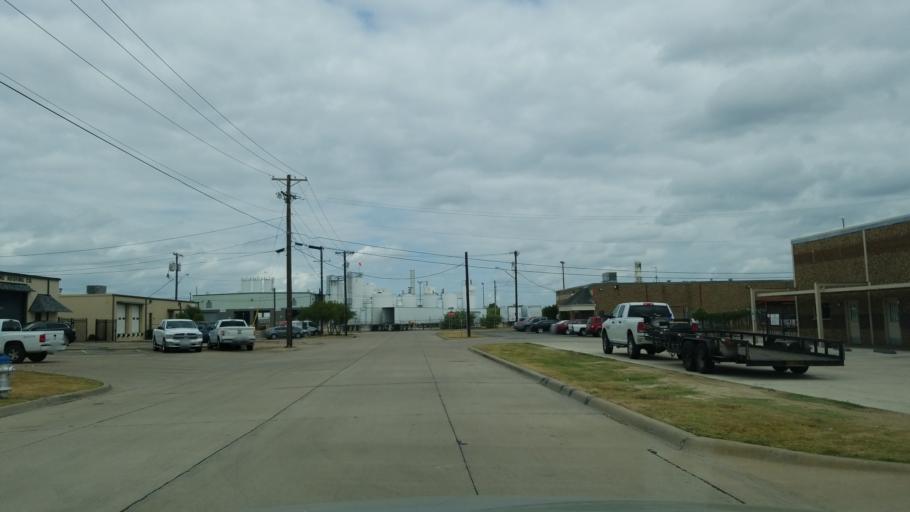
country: US
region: Texas
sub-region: Dallas County
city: Garland
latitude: 32.8856
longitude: -96.6757
